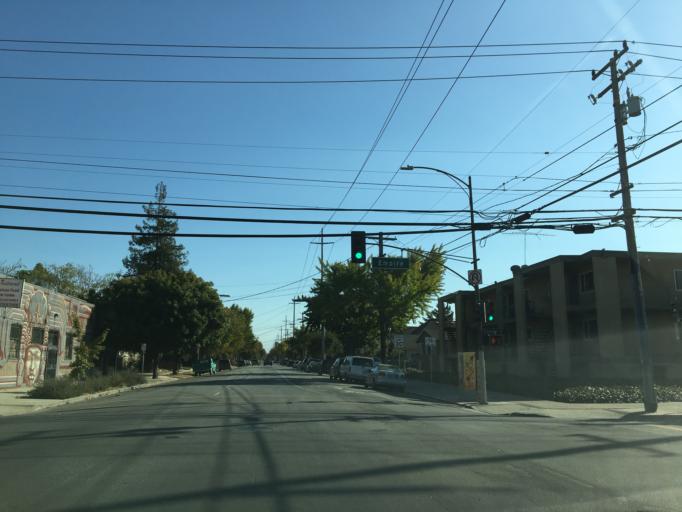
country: US
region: California
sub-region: Santa Clara County
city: San Jose
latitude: 37.3495
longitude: -121.8876
